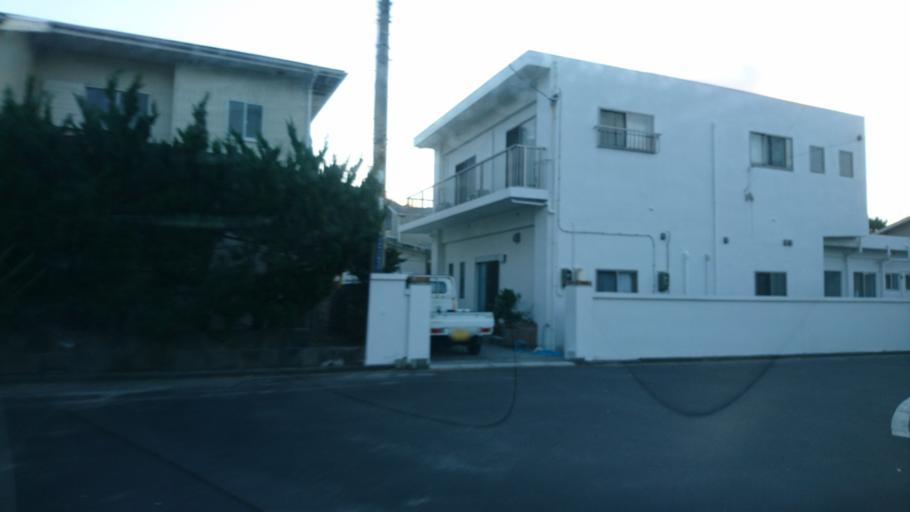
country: JP
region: Shizuoka
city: Shimoda
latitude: 34.3724
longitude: 139.2532
